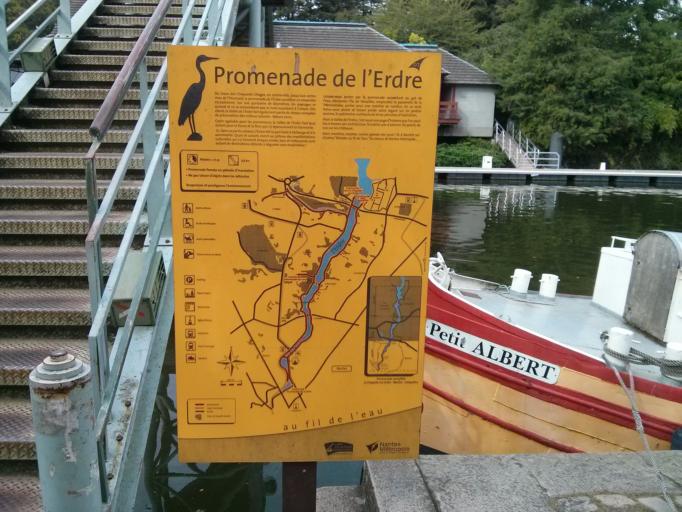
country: FR
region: Pays de la Loire
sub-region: Departement de la Loire-Atlantique
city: Nantes
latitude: 47.2253
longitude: -1.5532
